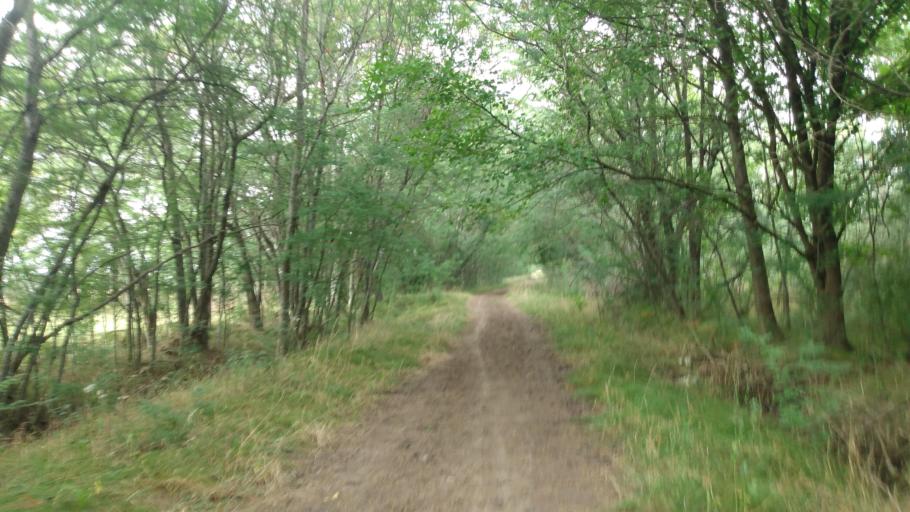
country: AR
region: Buenos Aires
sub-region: Partido de Lujan
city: Lujan
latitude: -34.6006
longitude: -59.0634
